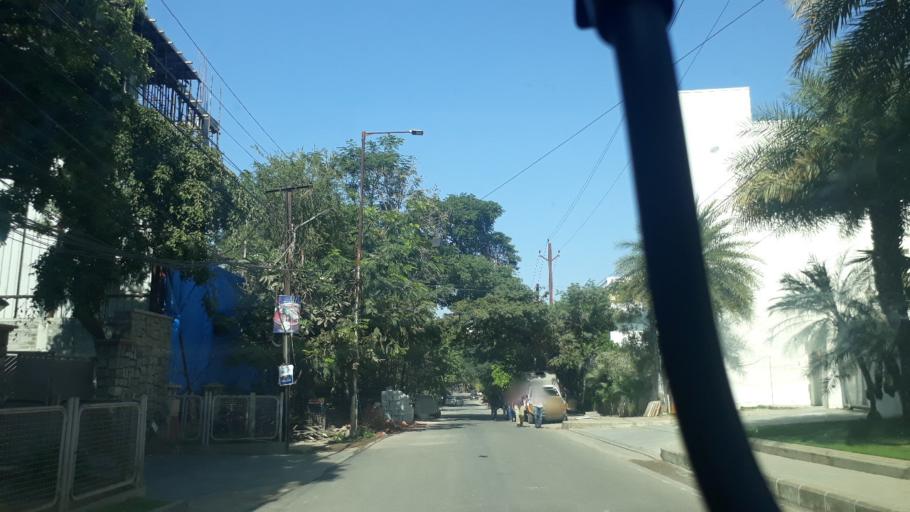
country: IN
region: Telangana
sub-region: Rangareddi
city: Kukatpalli
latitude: 17.4288
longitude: 78.4066
